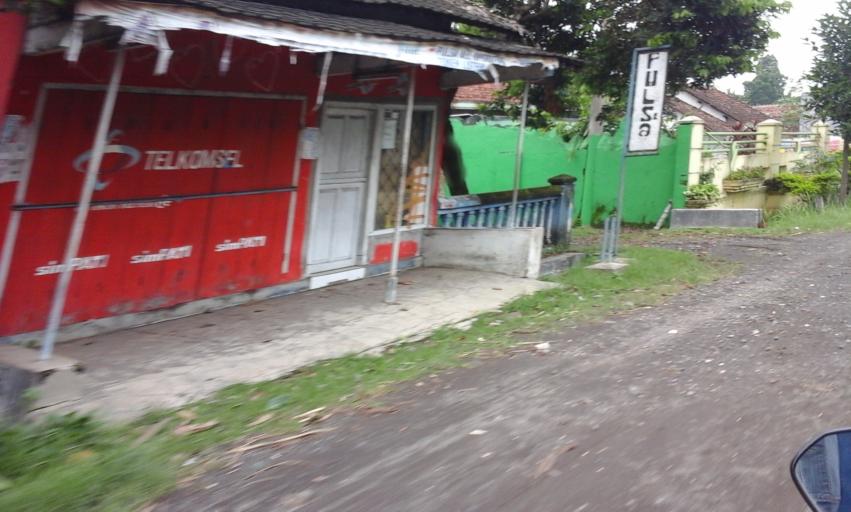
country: ID
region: East Java
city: Gambirono
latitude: -8.1995
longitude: 113.5227
